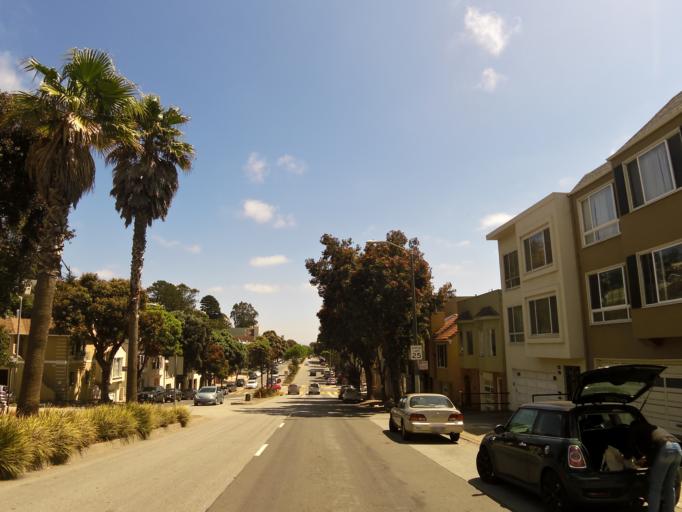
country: US
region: California
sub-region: San Mateo County
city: Daly City
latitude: 37.7315
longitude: -122.4476
